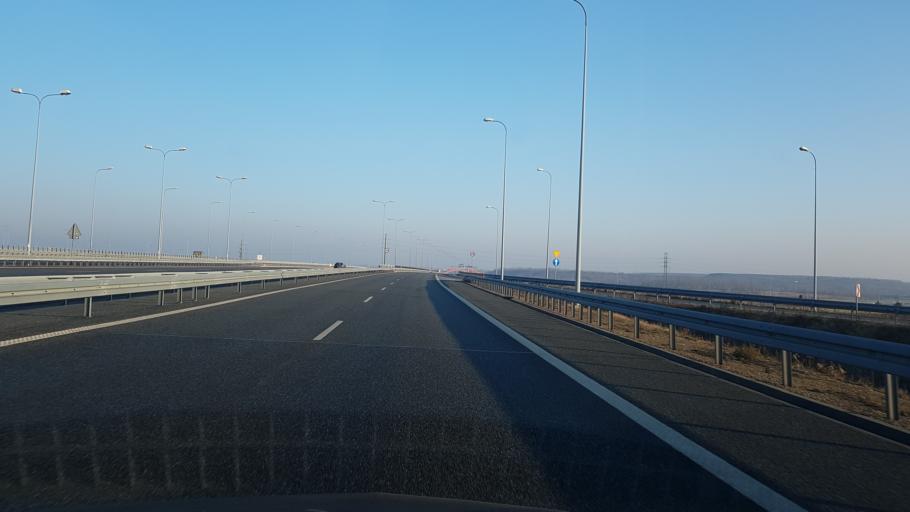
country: PL
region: Silesian Voivodeship
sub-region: Powiat gliwicki
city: Przyszowice
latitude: 50.2597
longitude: 18.7197
